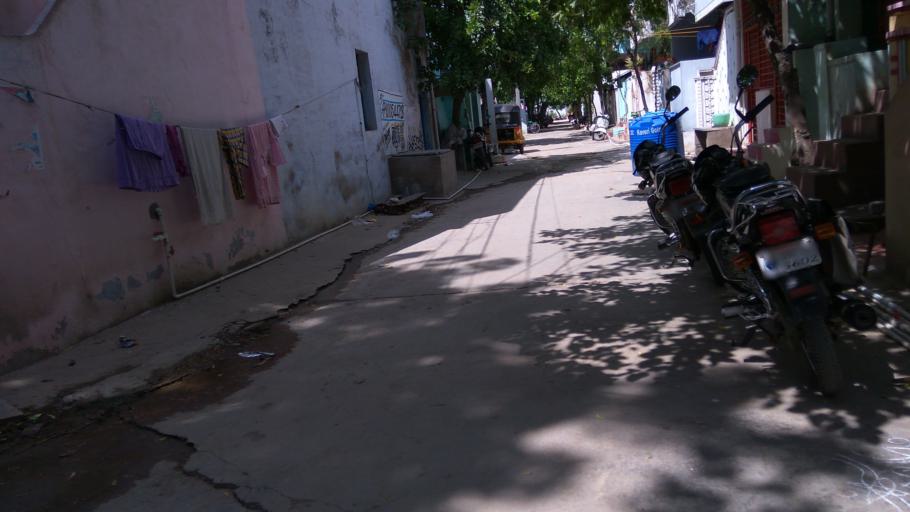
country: IN
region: Andhra Pradesh
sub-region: Prakasam
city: Markapur
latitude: 15.7438
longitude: 79.2706
